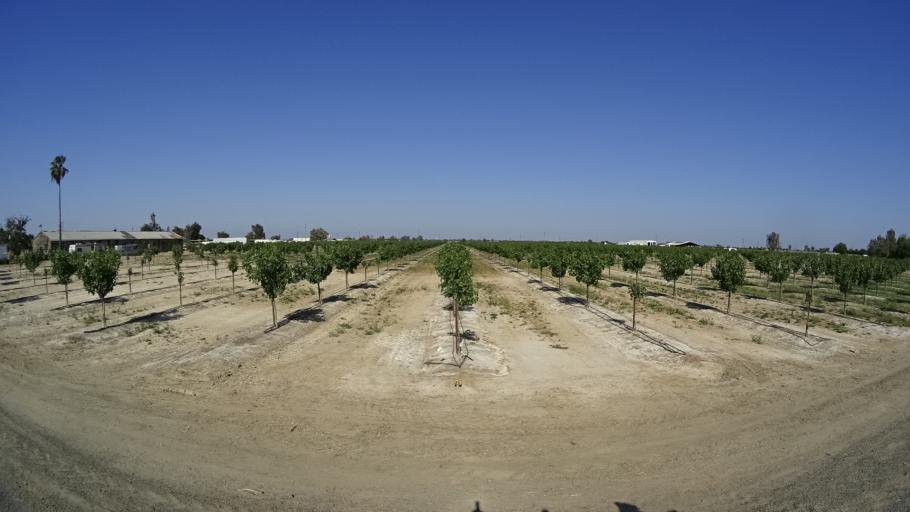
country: US
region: California
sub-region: Kings County
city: Home Garden
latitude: 36.3160
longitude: -119.5831
